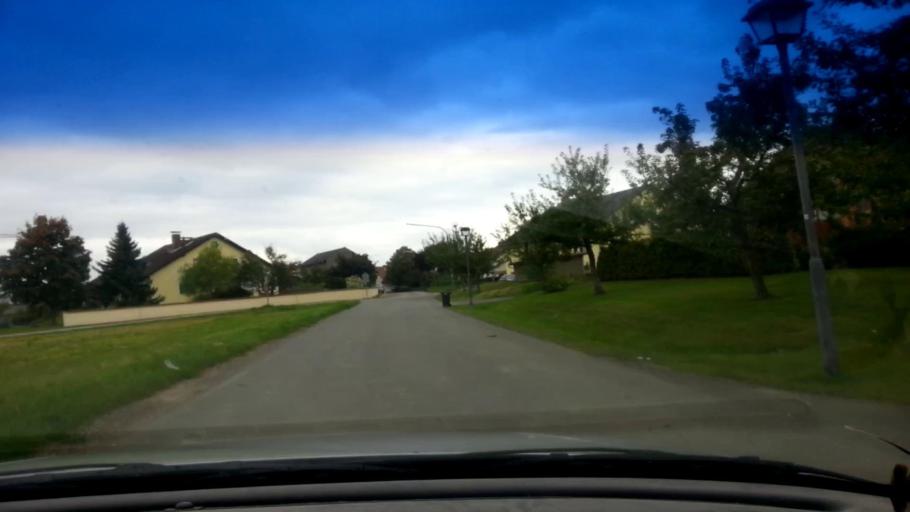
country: DE
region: Bavaria
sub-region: Upper Franconia
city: Zapfendorf
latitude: 49.9904
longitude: 10.9453
